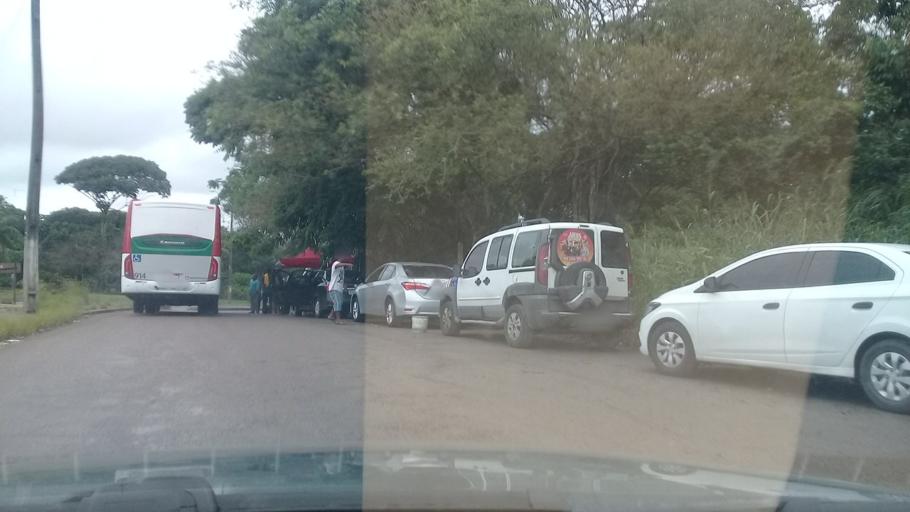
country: BR
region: Pernambuco
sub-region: Jaboatao Dos Guararapes
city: Jaboatao dos Guararapes
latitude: -8.0632
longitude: -34.9832
